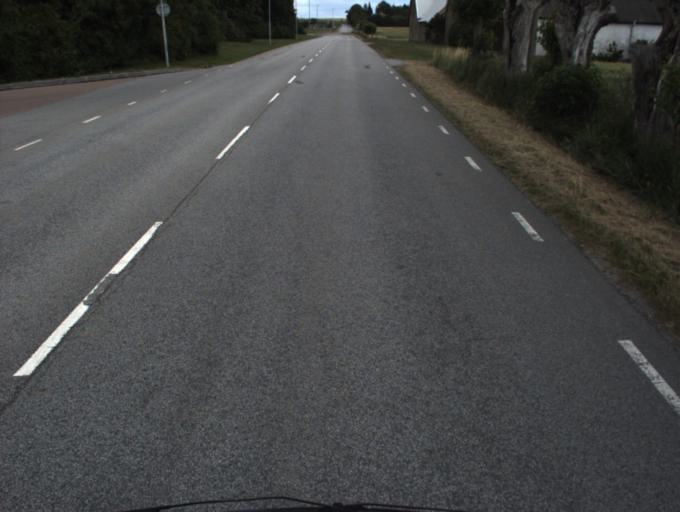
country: SE
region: Skane
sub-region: Helsingborg
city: Rydeback
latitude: 55.9581
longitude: 12.7757
